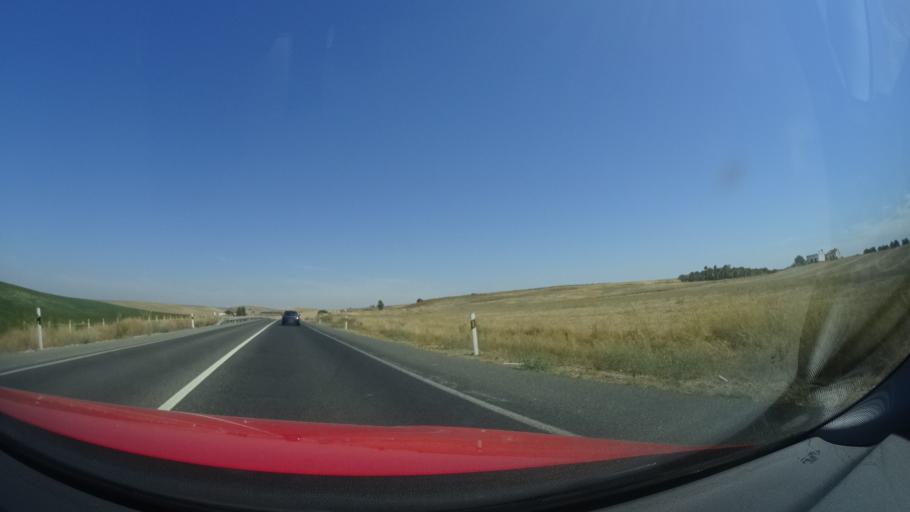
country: ES
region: Andalusia
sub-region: Provincia de Sevilla
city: Las Cabezas de San Juan
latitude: 36.9552
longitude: -5.8967
